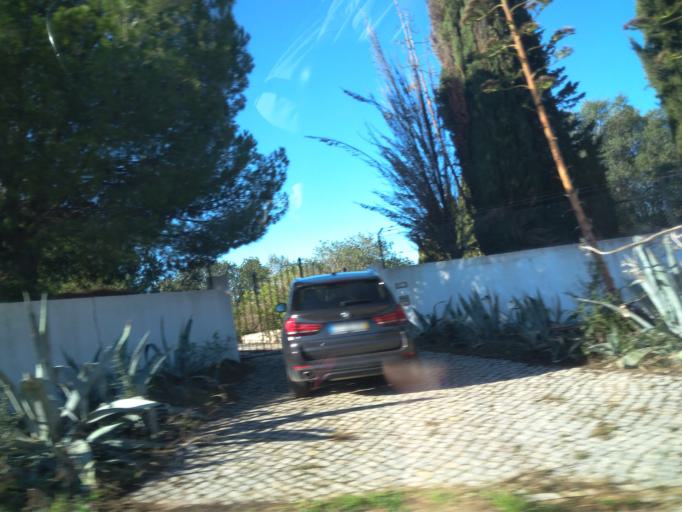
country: PT
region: Faro
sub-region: Faro
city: Santa Barbara de Nexe
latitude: 37.0940
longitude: -7.9628
